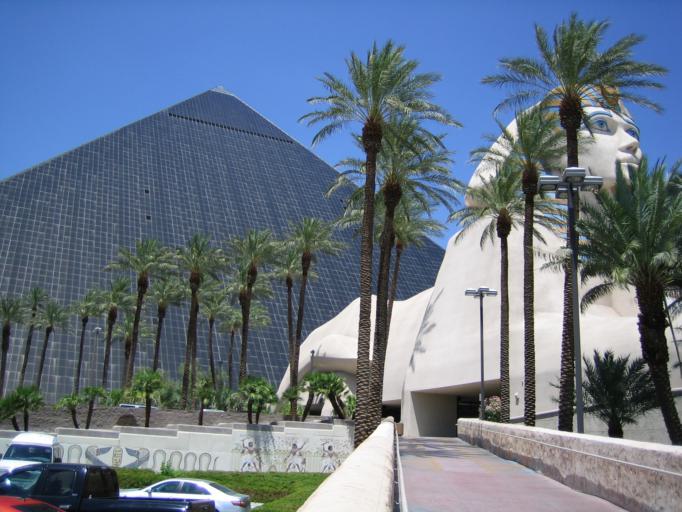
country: US
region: Nevada
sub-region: Clark County
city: Paradise
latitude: 36.0951
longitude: -115.1737
